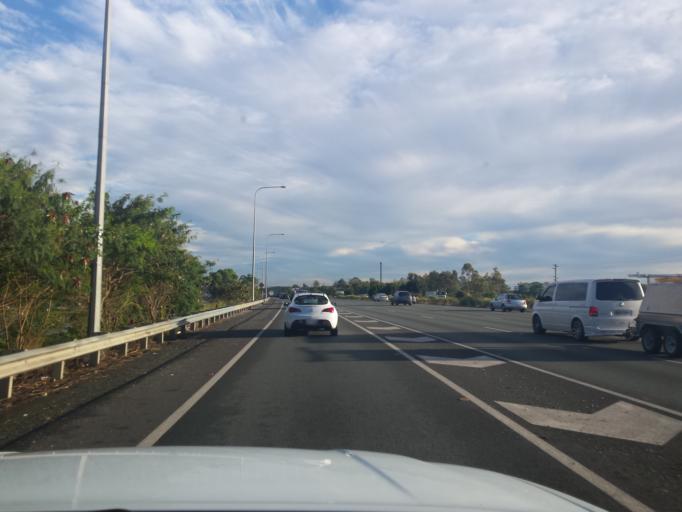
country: AU
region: Queensland
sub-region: Gold Coast
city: Oxenford
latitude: -27.8816
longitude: 153.3151
